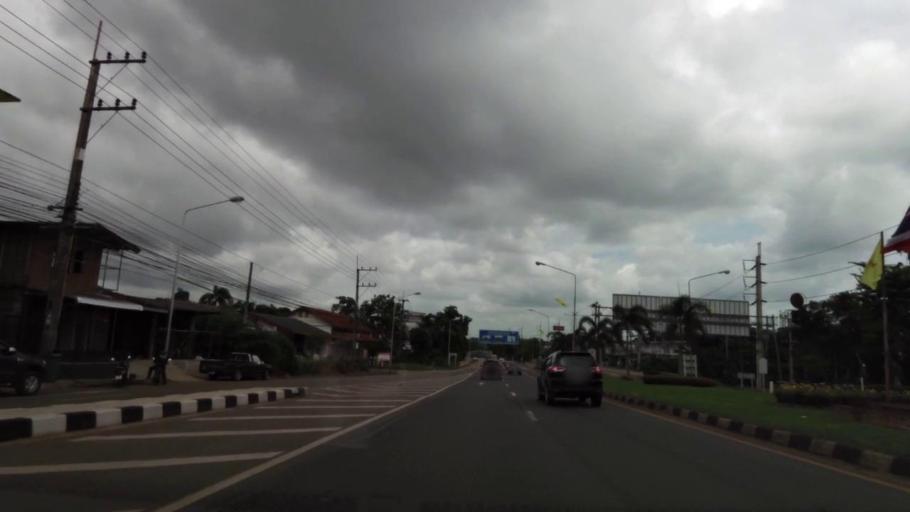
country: TH
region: Chanthaburi
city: Na Yai Am
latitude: 12.7798
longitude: 101.8215
